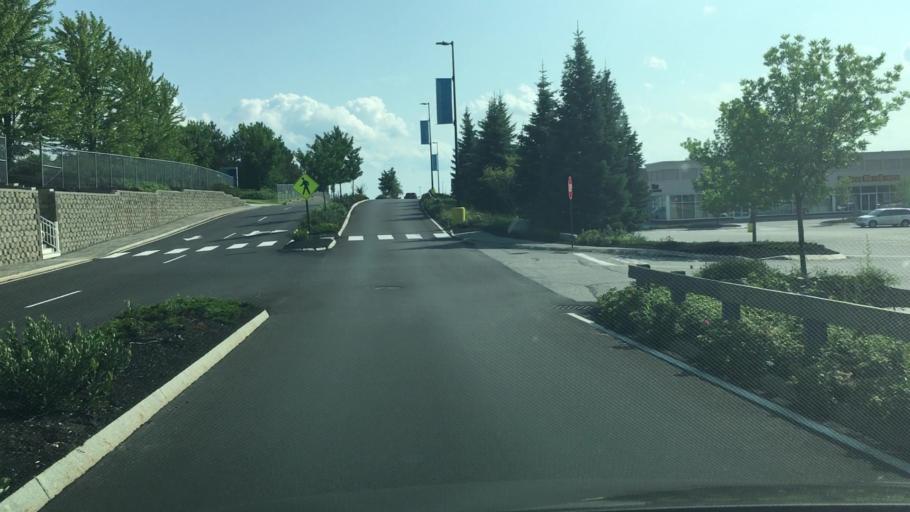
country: US
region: Maine
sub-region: Kennebec County
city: Augusta
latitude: 44.3469
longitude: -69.7886
